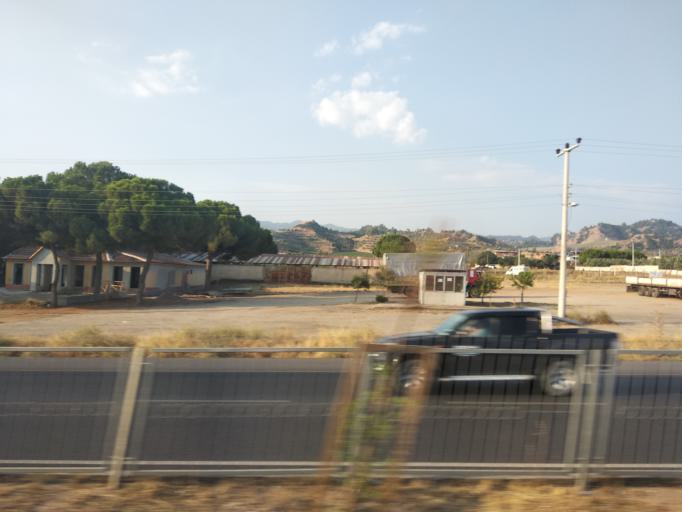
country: TR
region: Manisa
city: Ahmetli
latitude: 38.5051
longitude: 28.0036
